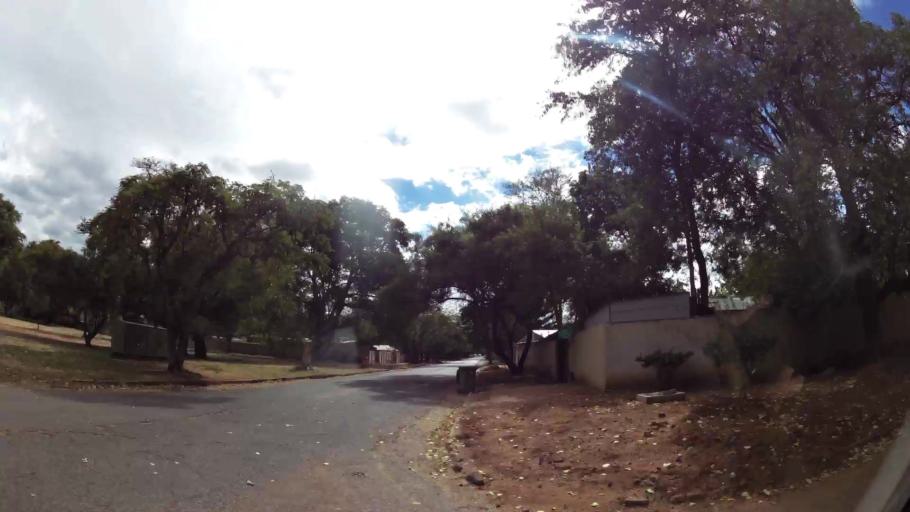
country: ZA
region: Limpopo
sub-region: Waterberg District Municipality
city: Warmbaths
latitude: -24.8859
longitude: 28.2806
